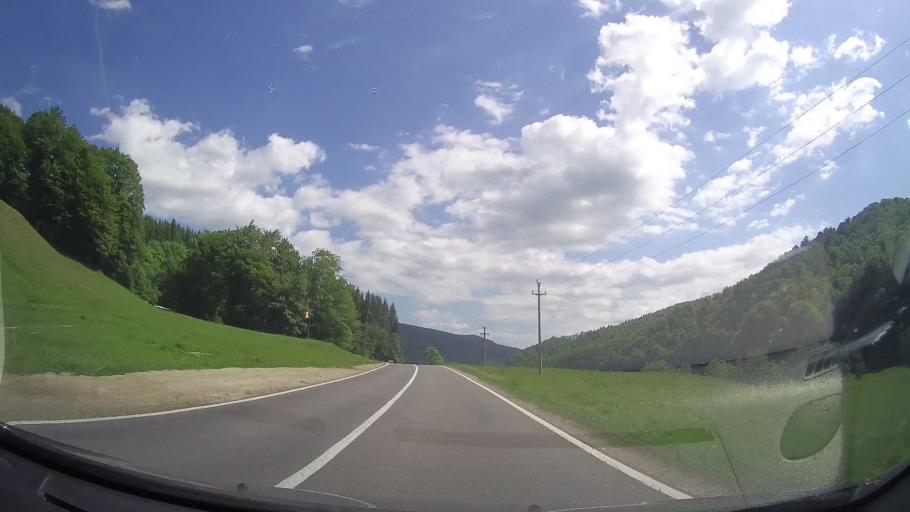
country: RO
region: Prahova
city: Maneciu
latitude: 45.4327
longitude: 25.9384
